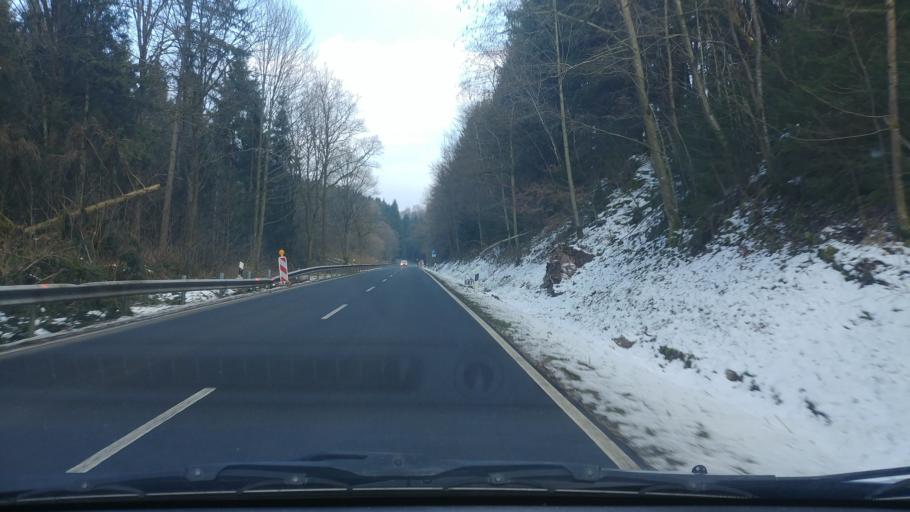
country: DE
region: Lower Saxony
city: Dassel
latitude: 51.7545
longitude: 9.6726
